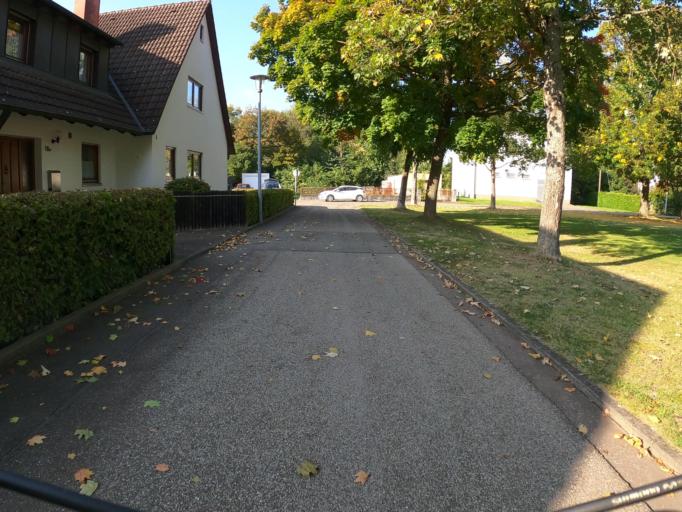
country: DE
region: Bavaria
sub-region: Swabia
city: Leipheim
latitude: 48.4526
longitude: 10.2268
